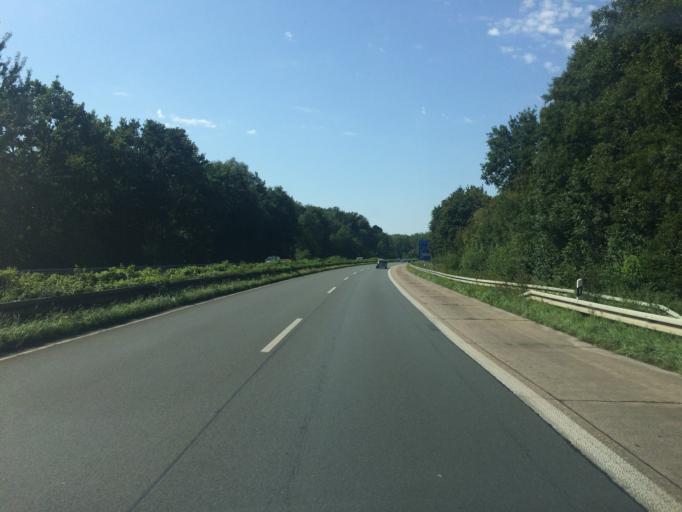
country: DE
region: North Rhine-Westphalia
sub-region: Regierungsbezirk Munster
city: Muenster
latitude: 51.9190
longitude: 7.5880
